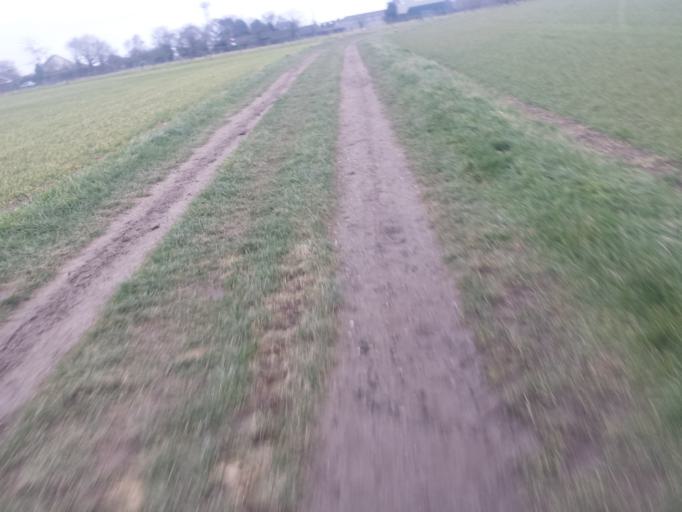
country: GB
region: England
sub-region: Essex
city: Little Clacton
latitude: 51.8544
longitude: 1.1599
